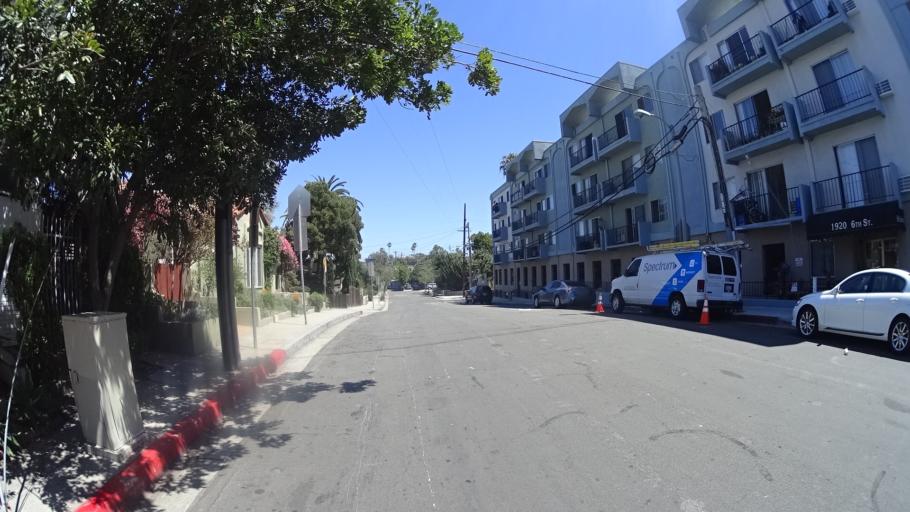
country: US
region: California
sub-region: Los Angeles County
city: Santa Monica
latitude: 34.0109
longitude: -118.4848
